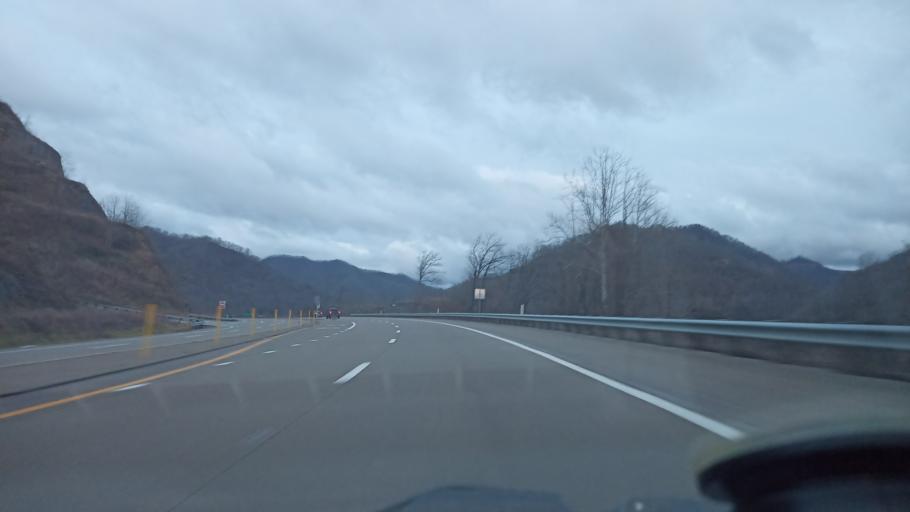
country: US
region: West Virginia
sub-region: Logan County
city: Logan
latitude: 37.7717
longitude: -81.9308
